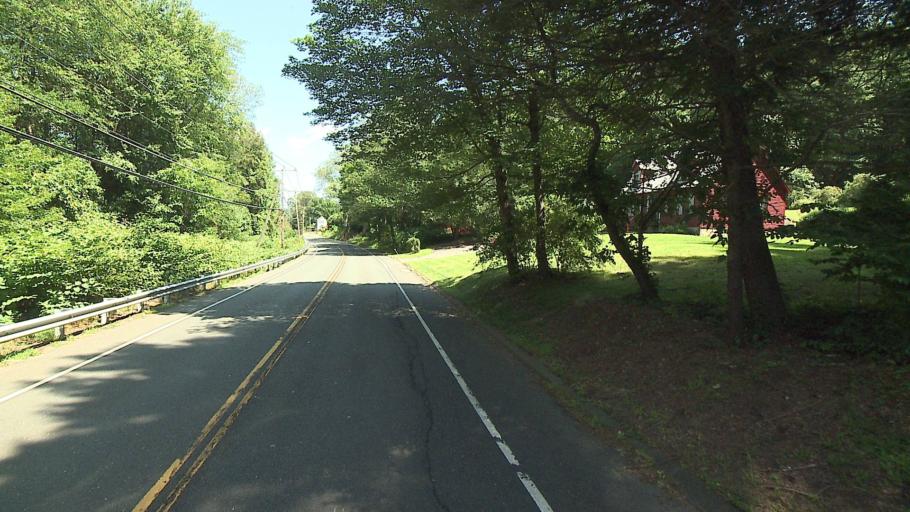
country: US
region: Connecticut
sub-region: Hartford County
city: Collinsville
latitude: 41.7789
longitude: -72.9346
